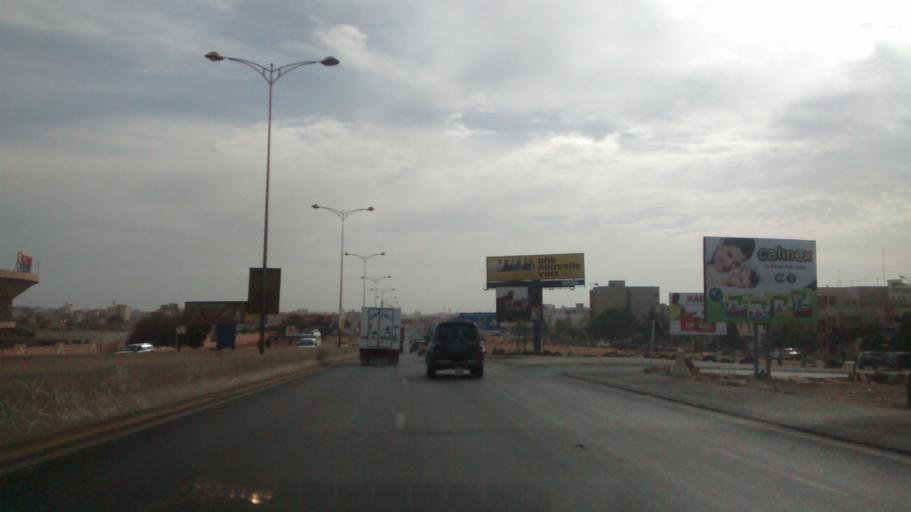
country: SN
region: Dakar
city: Grand Dakar
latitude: 14.7449
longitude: -17.4545
